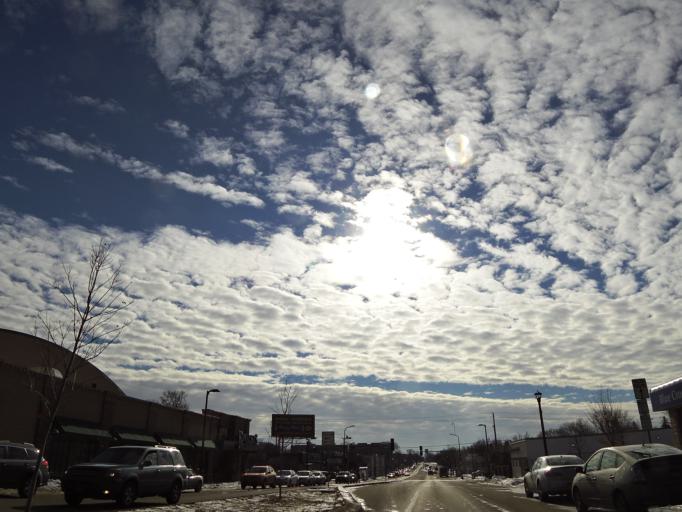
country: US
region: Minnesota
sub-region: Hennepin County
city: Richfield
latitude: 44.9061
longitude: -93.2883
